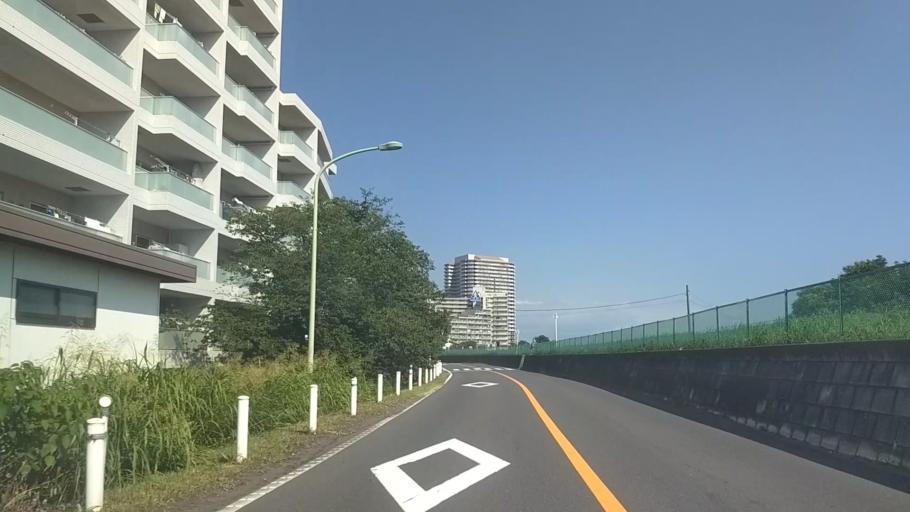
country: JP
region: Kanagawa
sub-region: Kawasaki-shi
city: Kawasaki
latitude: 35.5572
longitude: 139.6983
